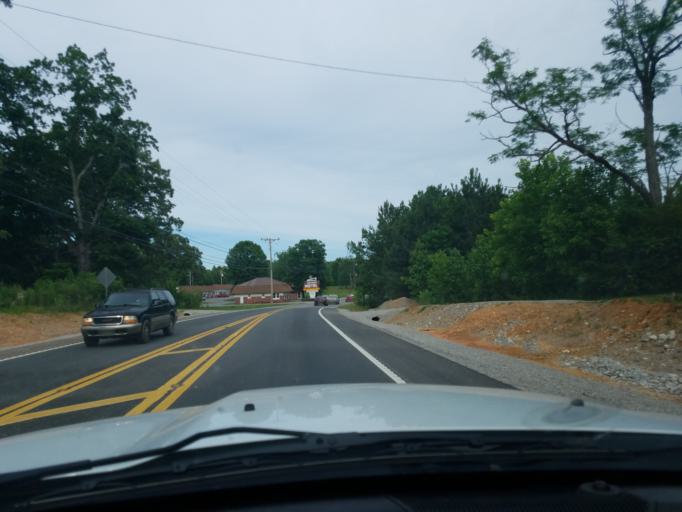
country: US
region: Tennessee
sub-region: Putnam County
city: Cookeville
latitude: 36.1773
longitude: -85.5598
